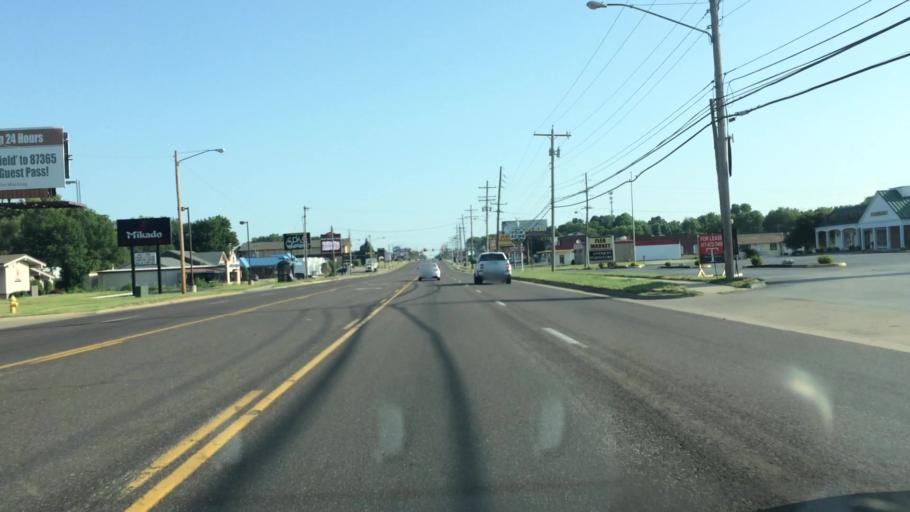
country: US
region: Missouri
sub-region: Greene County
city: Springfield
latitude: 37.1682
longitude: -93.2955
